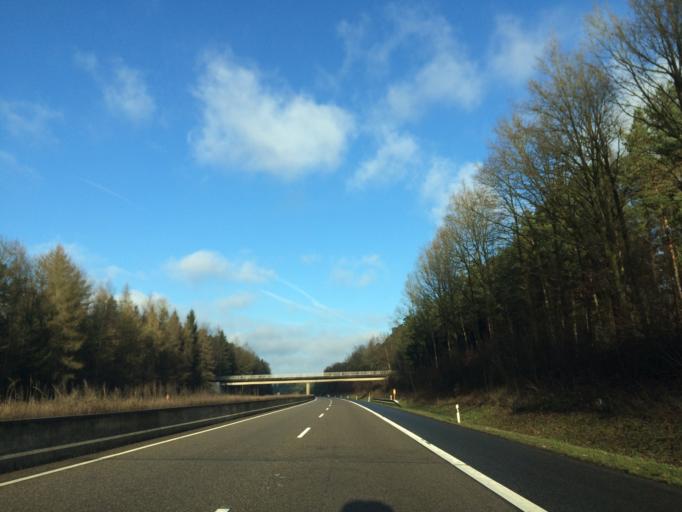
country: DE
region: Hesse
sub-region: Regierungsbezirk Kassel
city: Niederaula
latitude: 50.7375
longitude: 9.6423
